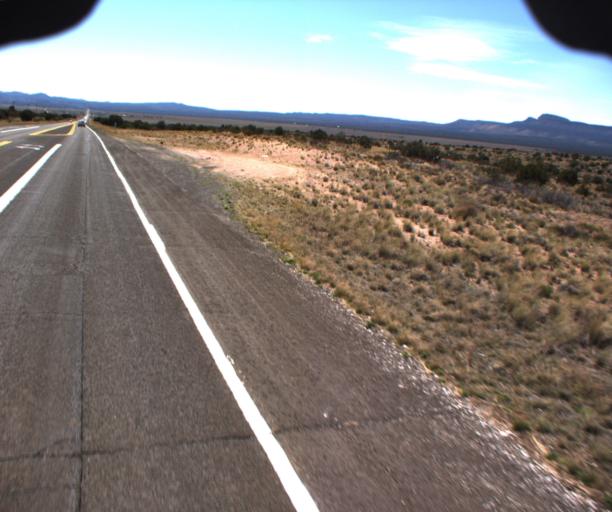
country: US
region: Arizona
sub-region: Mohave County
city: Peach Springs
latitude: 35.5021
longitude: -113.5279
